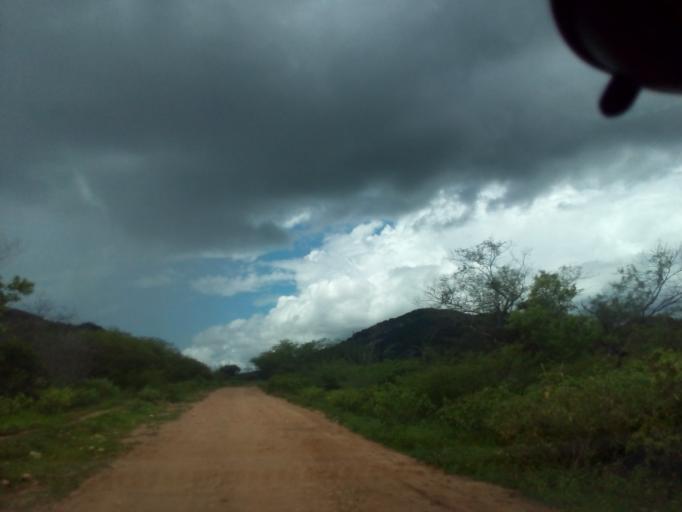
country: BR
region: Rio Grande do Norte
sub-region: Sao Paulo Do Potengi
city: Sao Paulo do Potengi
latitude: -5.9507
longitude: -35.9136
